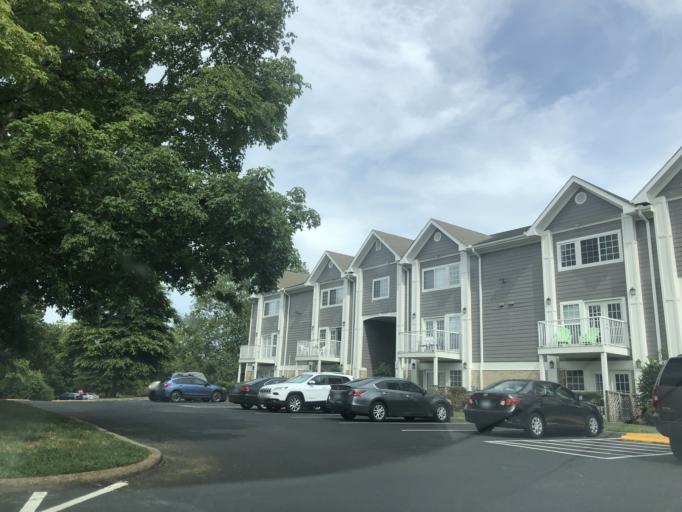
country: US
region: Tennessee
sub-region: Davidson County
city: Belle Meade
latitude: 36.0741
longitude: -86.9427
